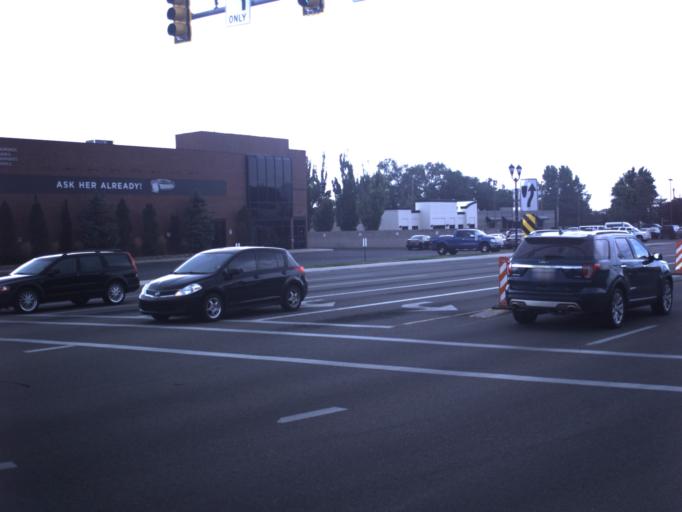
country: US
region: Utah
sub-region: Salt Lake County
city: Midvale
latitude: 40.6209
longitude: -111.8904
